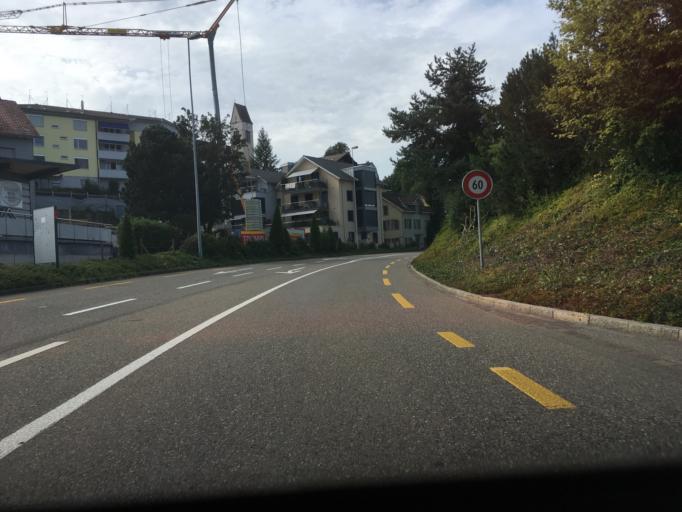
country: CH
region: Zurich
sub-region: Bezirk Horgen
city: Richterswil / Dorfkern
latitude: 47.2111
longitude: 8.7040
